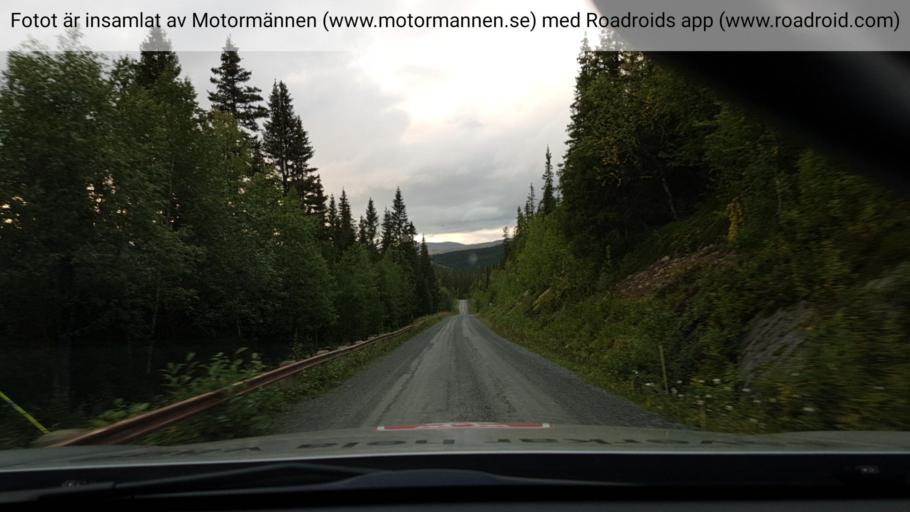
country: SE
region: Vaesterbotten
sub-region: Vilhelmina Kommun
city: Sjoberg
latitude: 65.4971
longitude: 15.4876
